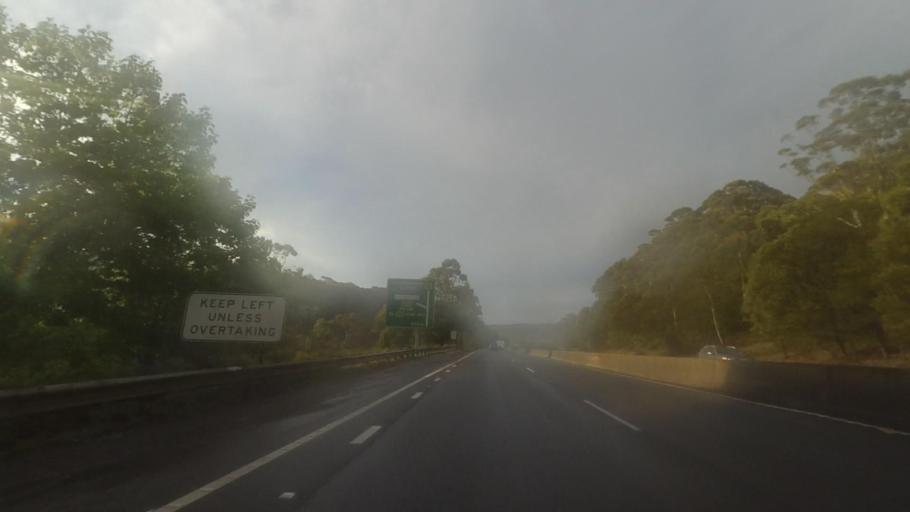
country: AU
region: New South Wales
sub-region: Wollongong
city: Mount Ousley
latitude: -34.3718
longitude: 150.8599
